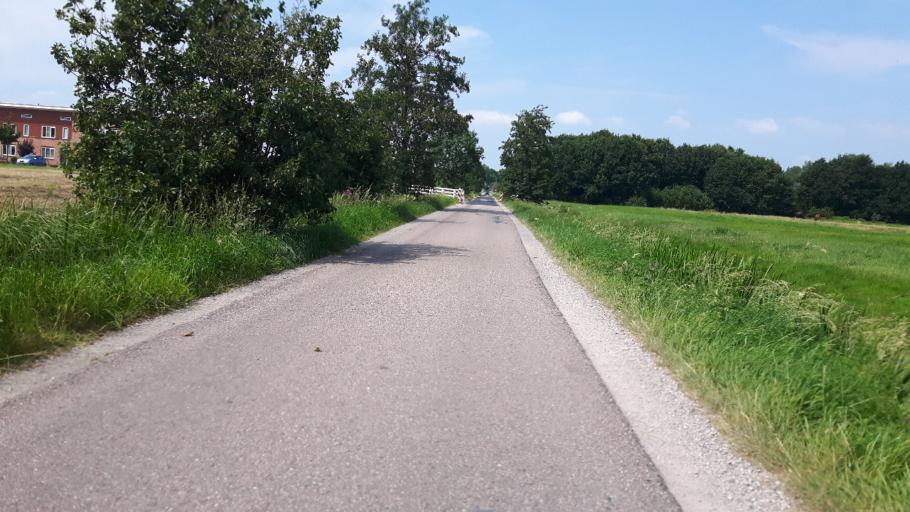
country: NL
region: South Holland
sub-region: Molenwaard
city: Liesveld
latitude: 51.9241
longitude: 4.8366
